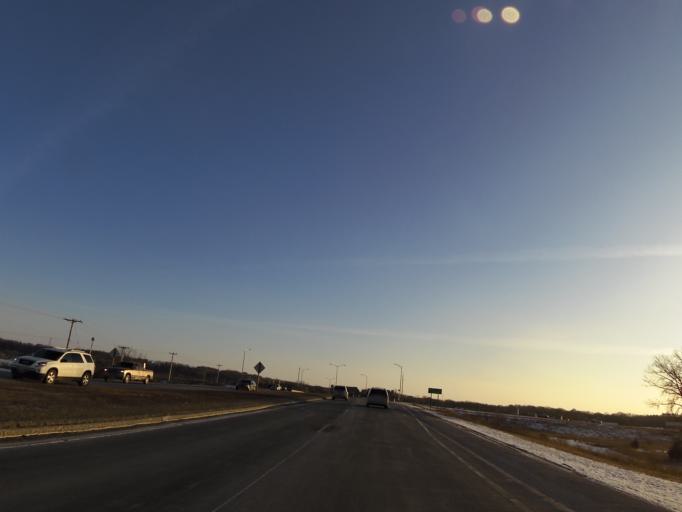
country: US
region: Wisconsin
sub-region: Saint Croix County
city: Hudson
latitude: 44.9662
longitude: -92.6804
